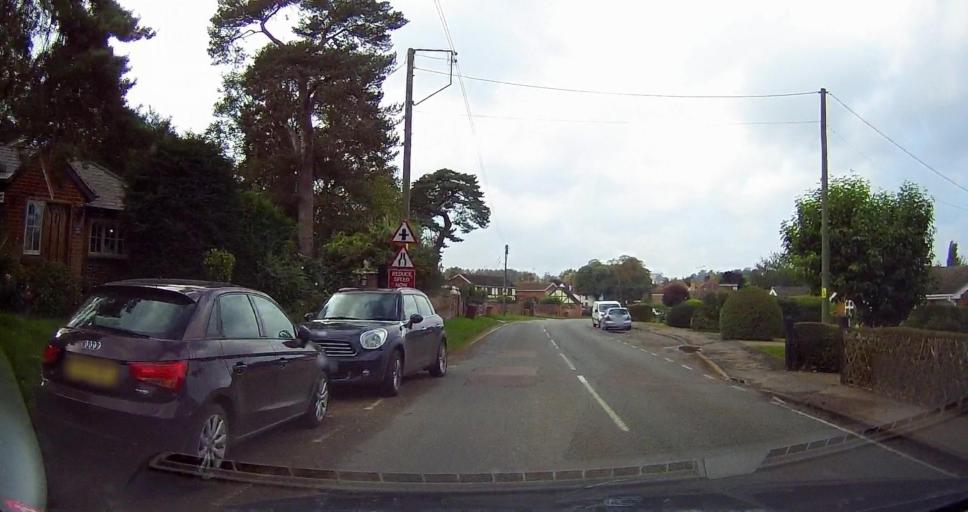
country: GB
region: England
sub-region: Kent
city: Longfield
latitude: 51.4205
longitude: 0.3097
